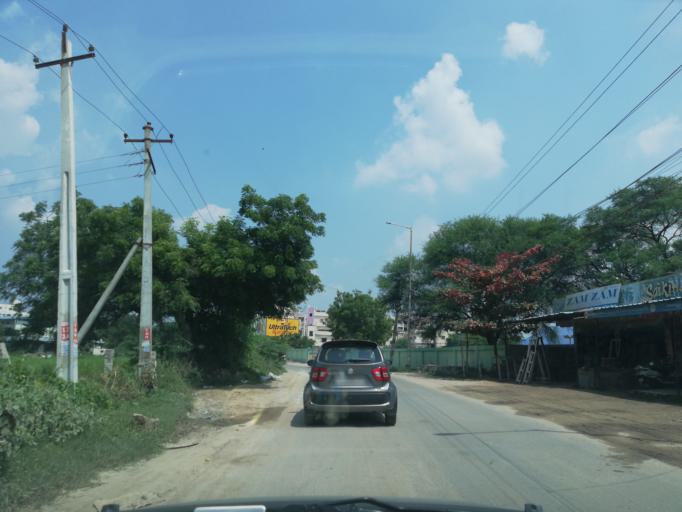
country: IN
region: Telangana
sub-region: Medak
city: Serilingampalle
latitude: 17.4877
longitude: 78.3203
